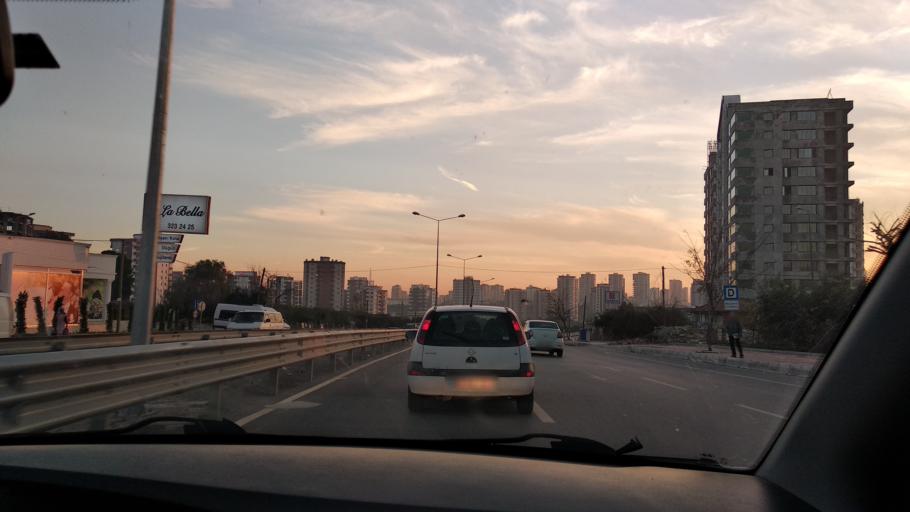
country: TR
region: Mersin
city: Mercin
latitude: 36.8175
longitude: 34.5962
